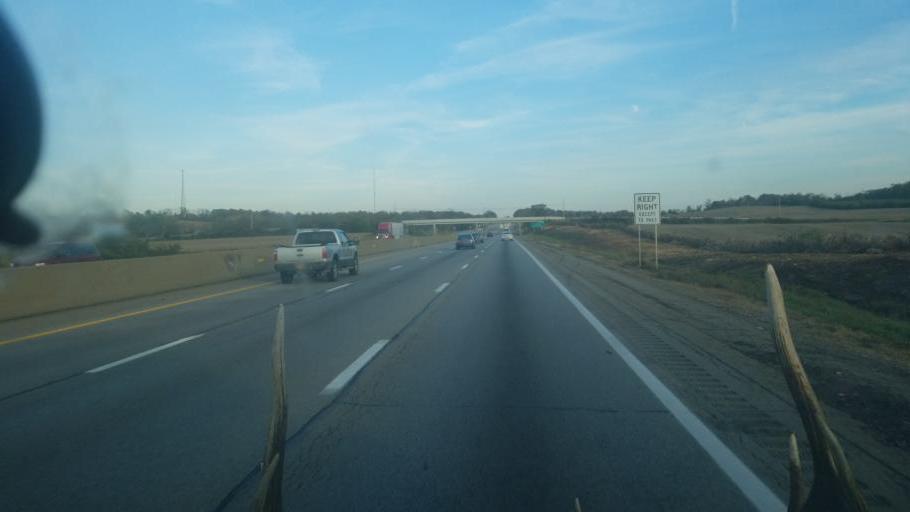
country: US
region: Ohio
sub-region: Licking County
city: Harbor Hills
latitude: 39.9450
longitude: -82.4274
